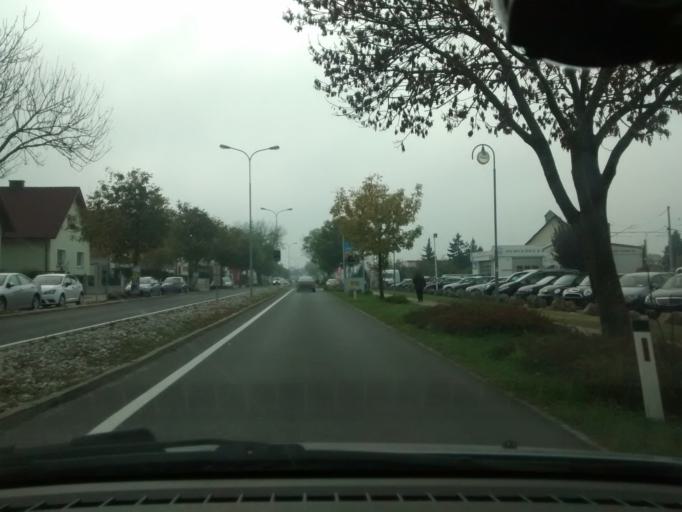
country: AT
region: Lower Austria
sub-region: Politischer Bezirk Baden
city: Traiskirchen
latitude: 48.0248
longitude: 16.2989
